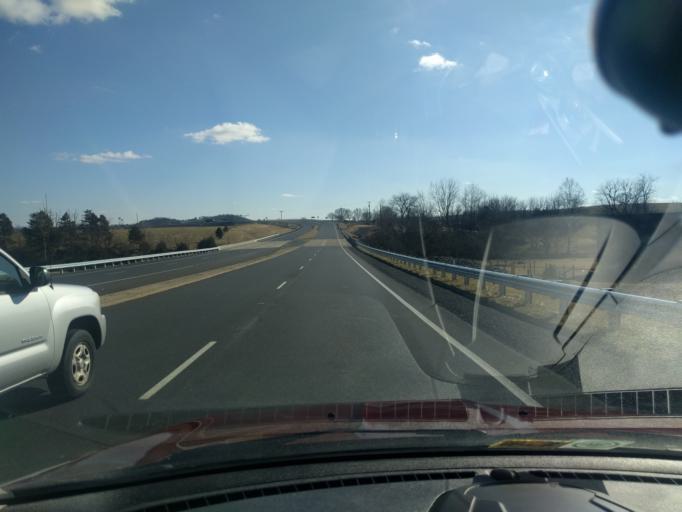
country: US
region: Virginia
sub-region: Rockingham County
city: Bridgewater
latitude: 38.3614
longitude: -78.9324
